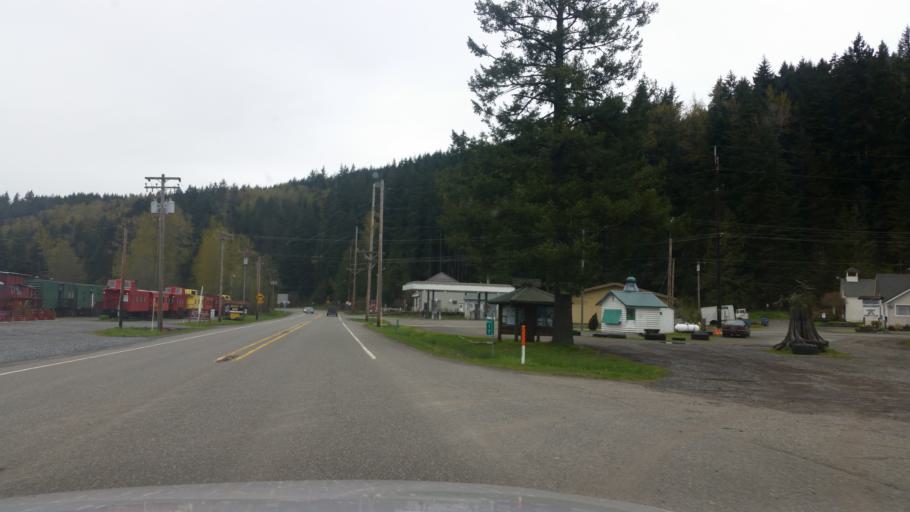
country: US
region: Washington
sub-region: Pierce County
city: Eatonville
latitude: 46.7653
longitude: -122.1942
